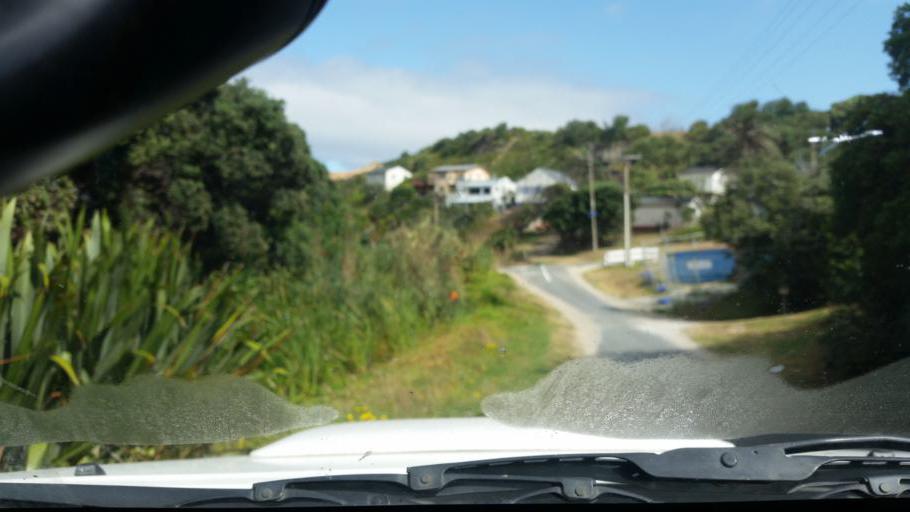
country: NZ
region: Northland
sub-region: Kaipara District
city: Dargaville
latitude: -35.9499
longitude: 173.7445
